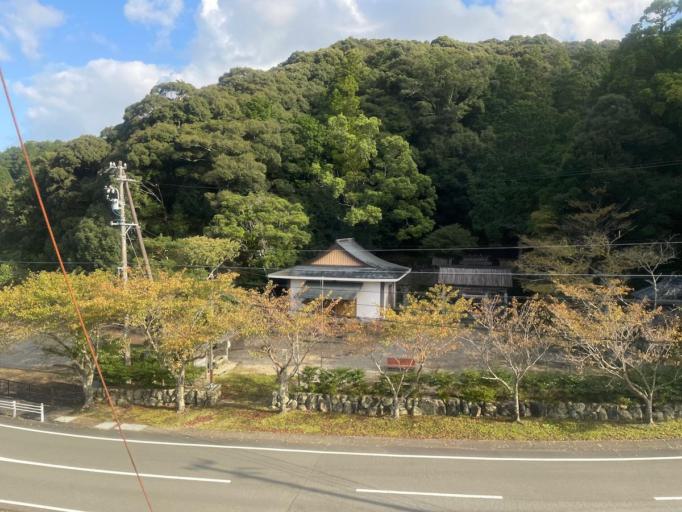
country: JP
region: Mie
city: Ise
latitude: 34.4773
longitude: 136.7608
